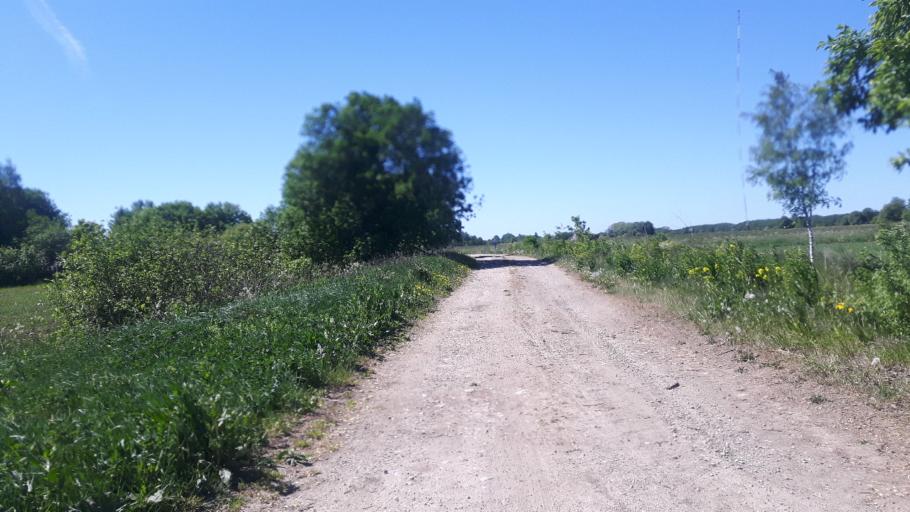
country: EE
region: Ida-Virumaa
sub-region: Toila vald
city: Voka
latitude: 59.4038
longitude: 27.6477
